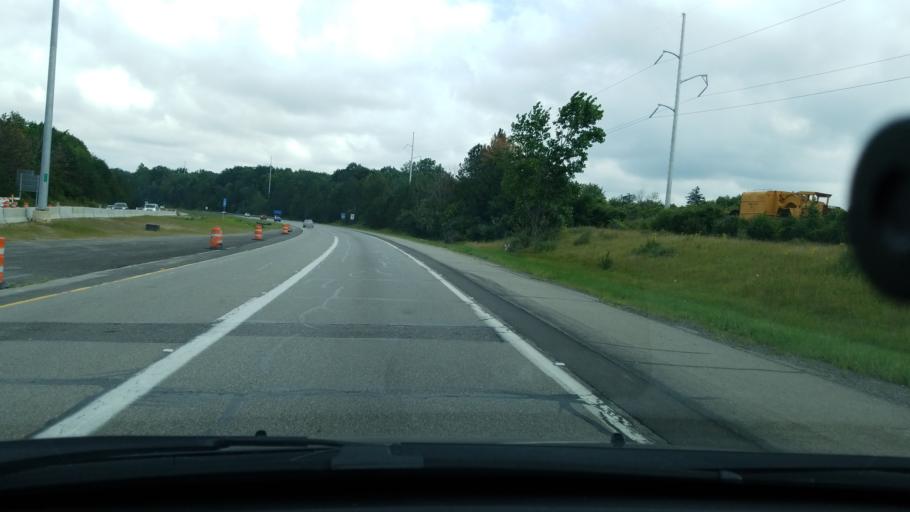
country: US
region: Ohio
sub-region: Lorain County
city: Sheffield
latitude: 41.4052
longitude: -82.1073
